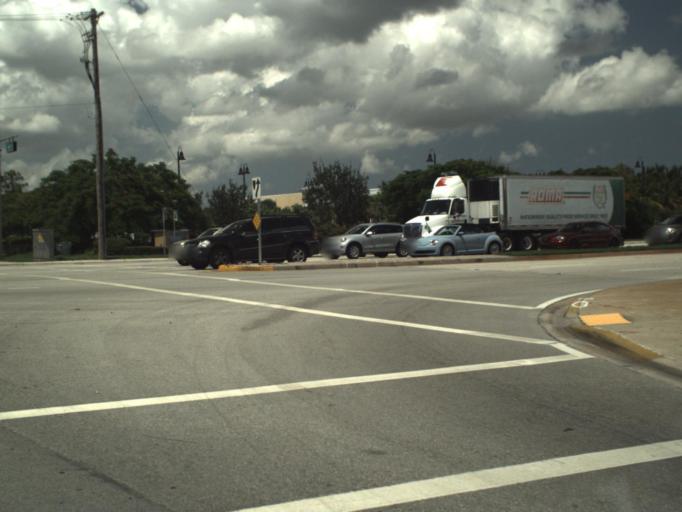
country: US
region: Florida
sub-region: Broward County
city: Parkland
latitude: 26.3173
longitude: -80.2024
